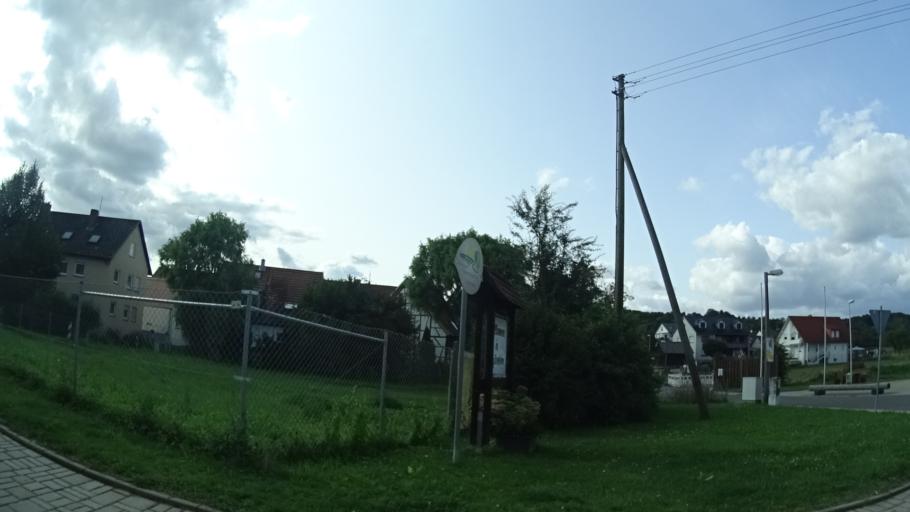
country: DE
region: Bavaria
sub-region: Regierungsbezirk Unterfranken
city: Greussenheim
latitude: 49.8136
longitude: 9.7689
